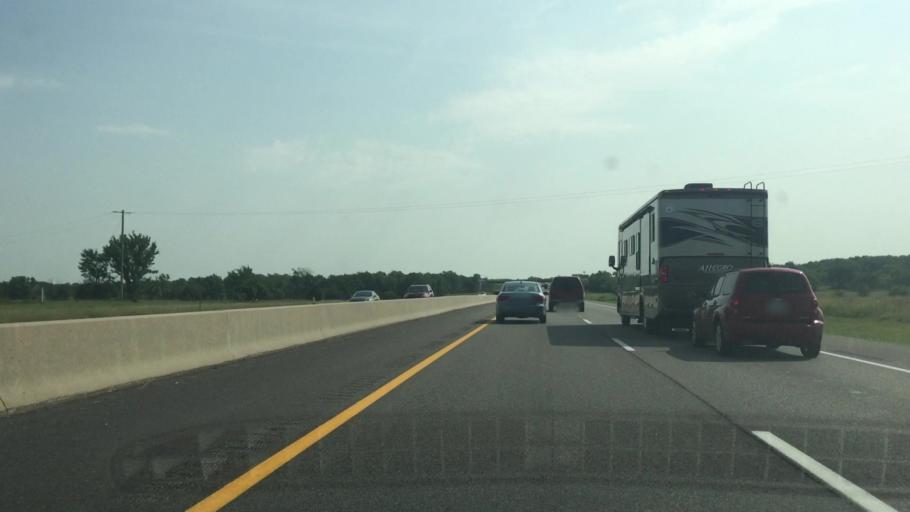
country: US
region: Kansas
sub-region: Butler County
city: Towanda
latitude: 37.7783
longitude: -96.9580
